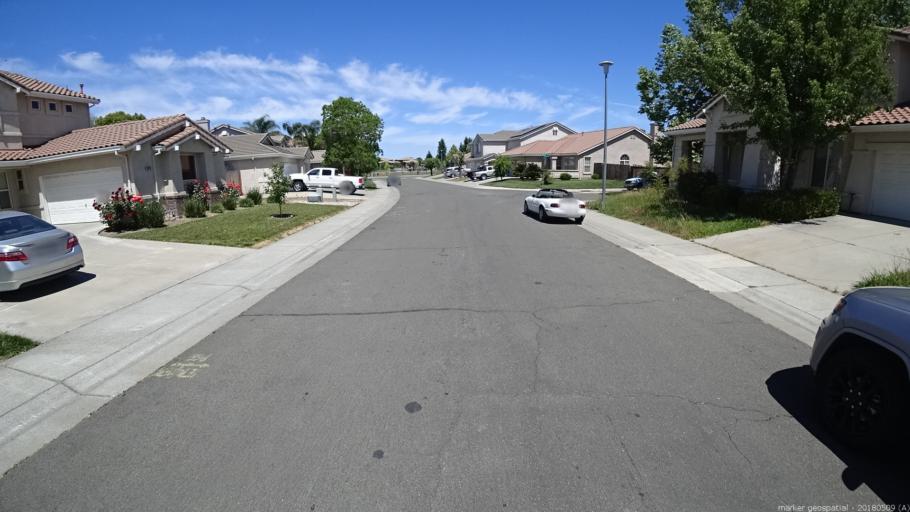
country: US
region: California
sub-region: Sacramento County
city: Sacramento
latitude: 38.6399
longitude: -121.5120
